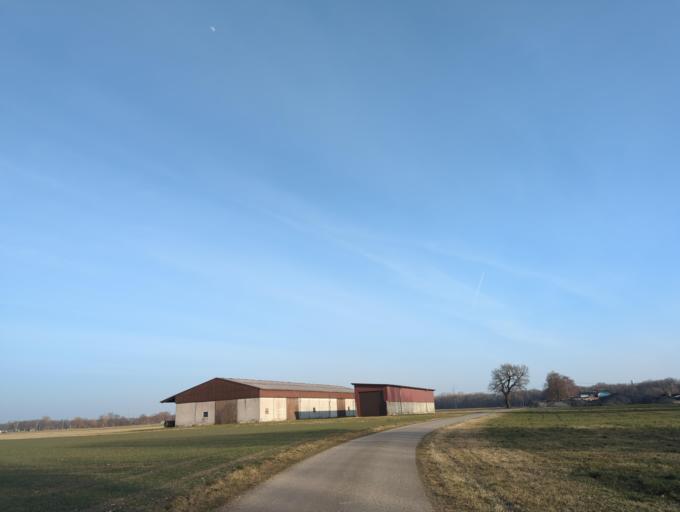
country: DE
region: Bavaria
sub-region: Swabia
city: Leipheim
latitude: 48.4640
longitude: 10.2122
